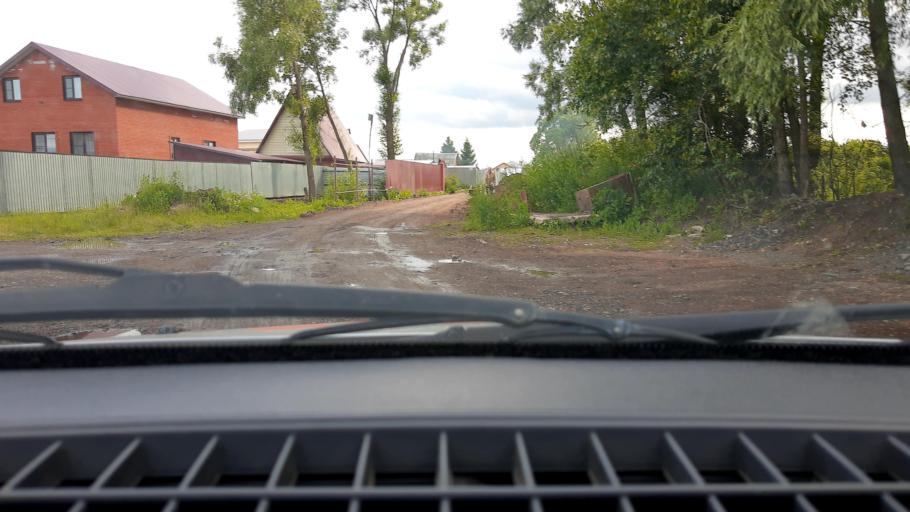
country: RU
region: Bashkortostan
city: Mikhaylovka
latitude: 54.7931
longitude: 55.8257
